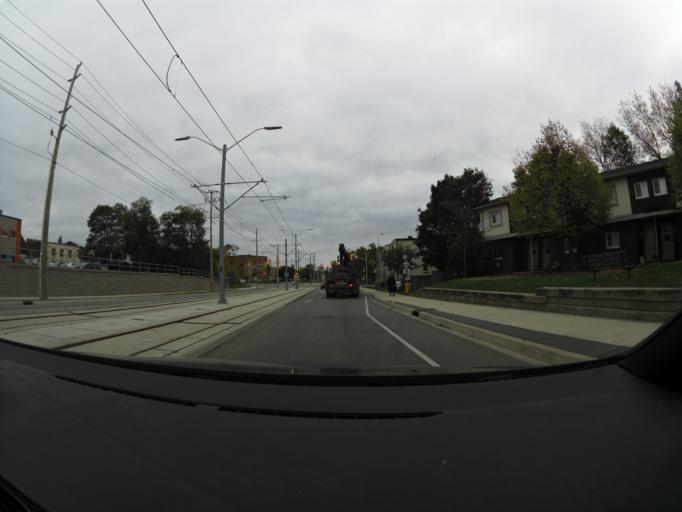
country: CA
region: Ontario
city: Kitchener
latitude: 43.4441
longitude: -80.4795
